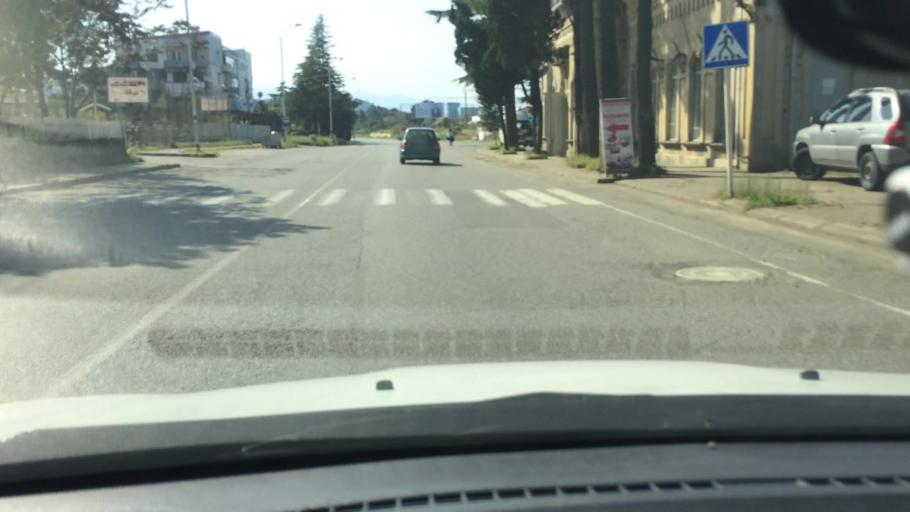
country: GE
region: Ajaria
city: Makhinjauri
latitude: 41.7340
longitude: 41.7330
